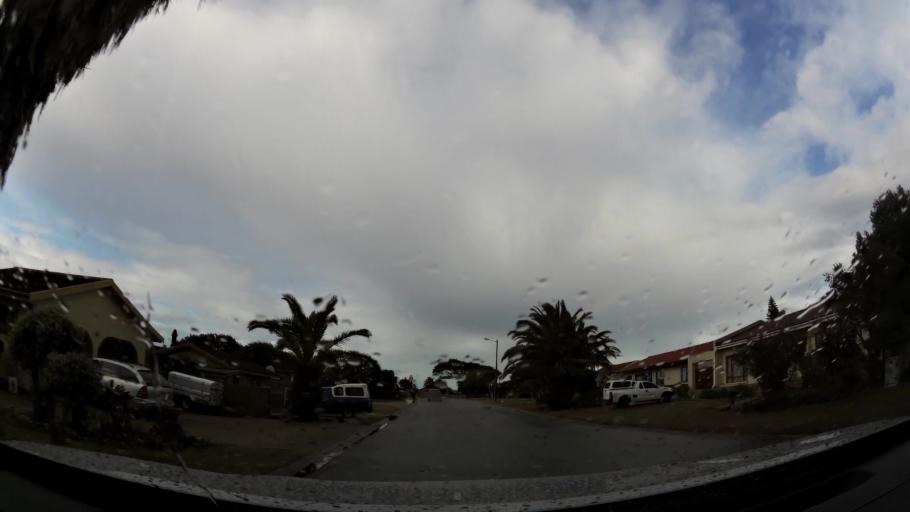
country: ZA
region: Western Cape
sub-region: Eden District Municipality
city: Mossel Bay
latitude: -34.1893
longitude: 22.1126
